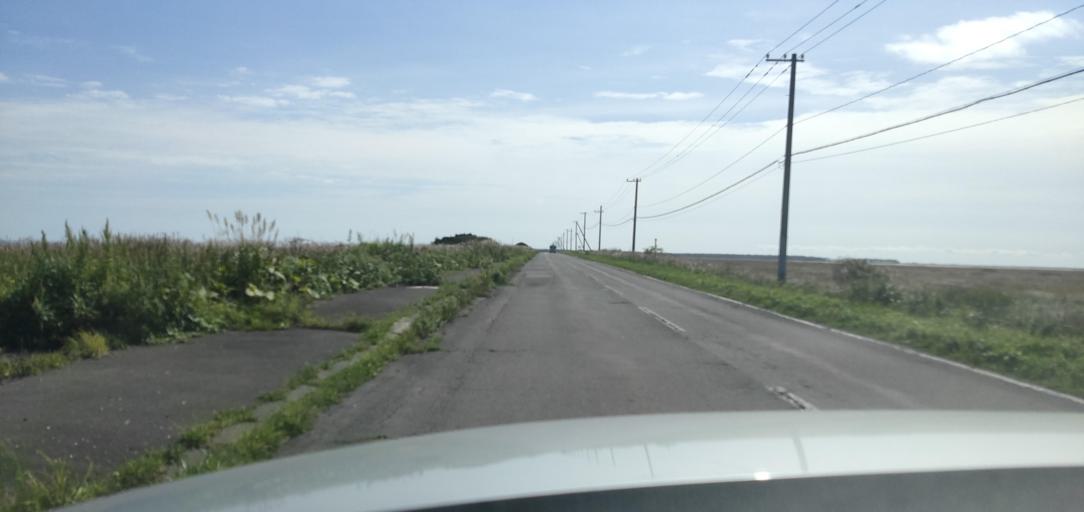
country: JP
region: Hokkaido
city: Shibetsu
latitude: 43.6197
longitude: 145.2282
